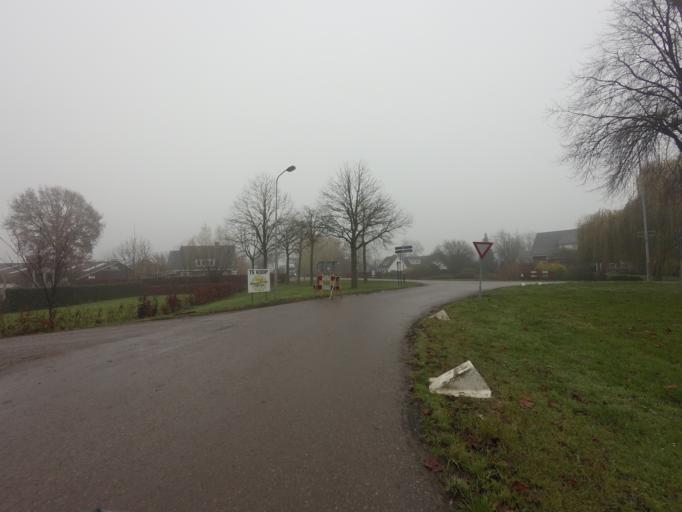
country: NL
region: Gelderland
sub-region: Gemeente Zaltbommel
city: Nederhemert-Noord
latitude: 51.7673
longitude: 5.1828
